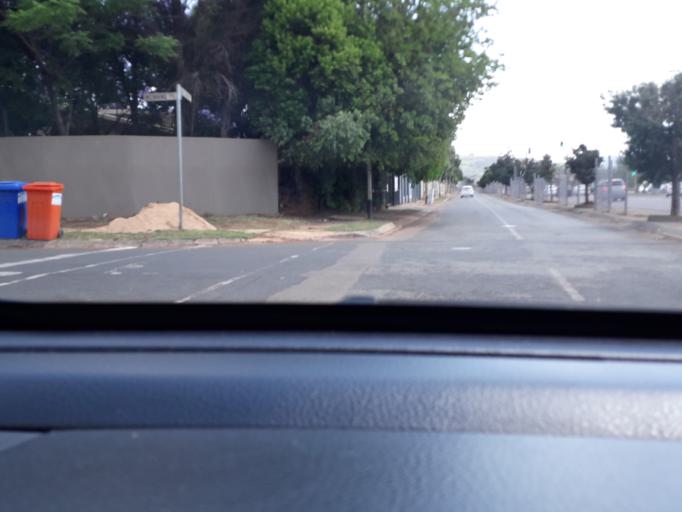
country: ZA
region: Gauteng
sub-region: City of Tshwane Metropolitan Municipality
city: Pretoria
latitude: -25.7714
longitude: 28.2112
